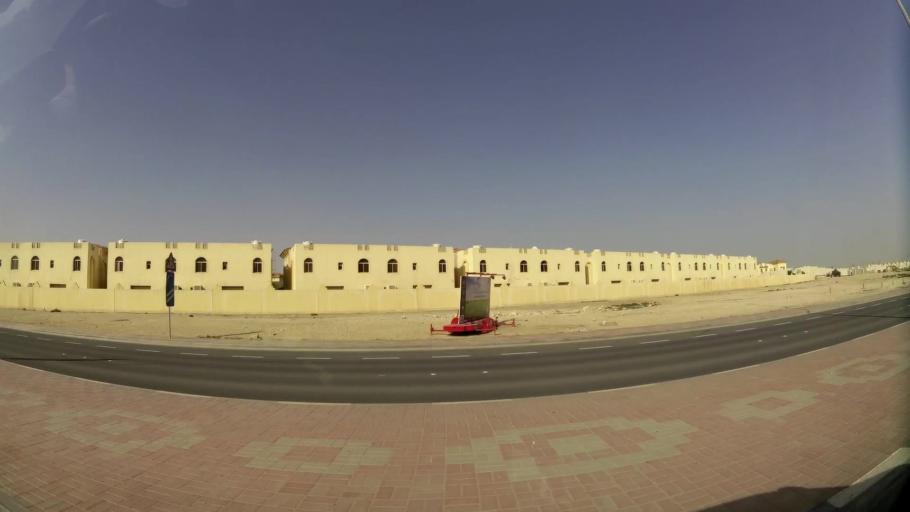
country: QA
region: Baladiyat ar Rayyan
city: Ar Rayyan
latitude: 25.3440
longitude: 51.4483
